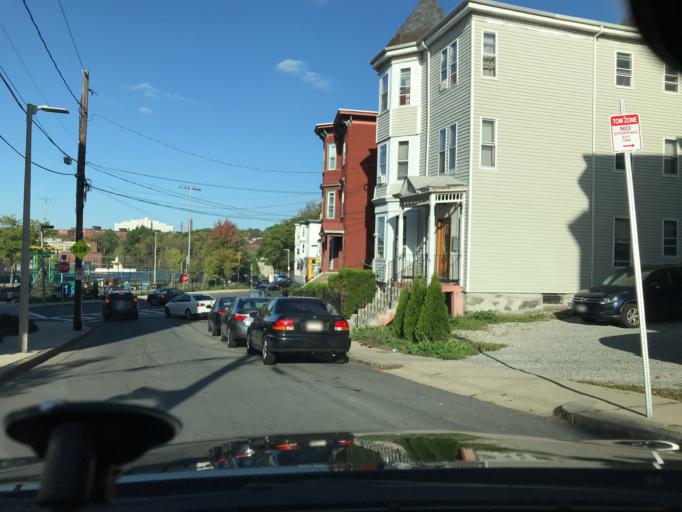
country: US
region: Massachusetts
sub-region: Norfolk County
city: Brookline
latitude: 42.3231
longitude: -71.0949
